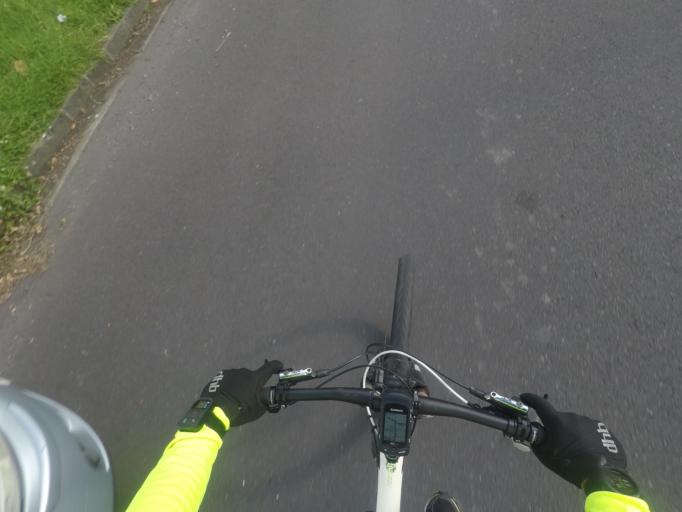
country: NZ
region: Auckland
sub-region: Auckland
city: Auckland
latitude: -36.8914
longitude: 174.7706
